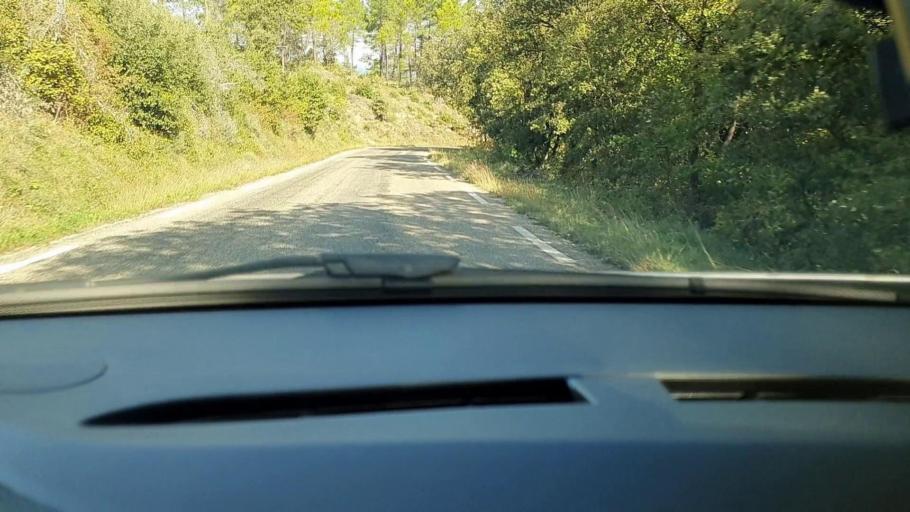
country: FR
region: Languedoc-Roussillon
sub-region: Departement du Gard
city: Saint-Florent-sur-Auzonnet
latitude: 44.2484
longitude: 4.1329
